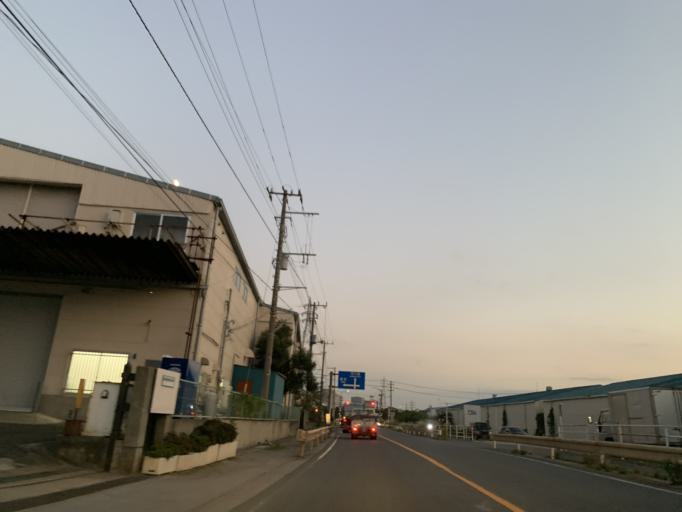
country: JP
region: Chiba
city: Funabashi
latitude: 35.6844
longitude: 139.9470
